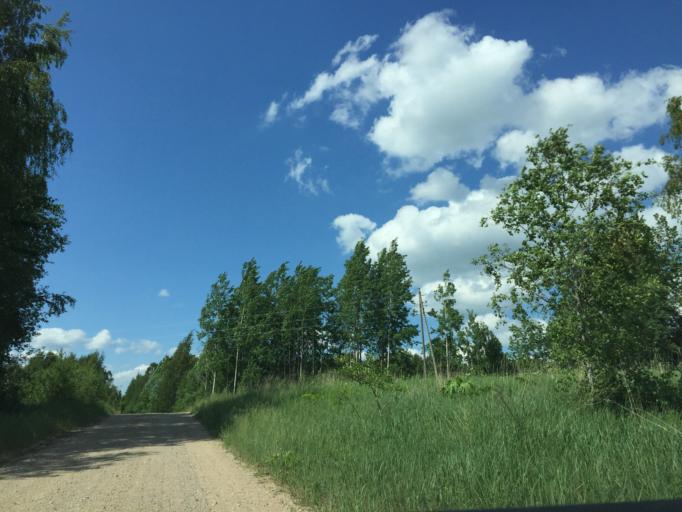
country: LV
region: Priekuli
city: Priekuli
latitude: 57.2557
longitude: 25.3897
